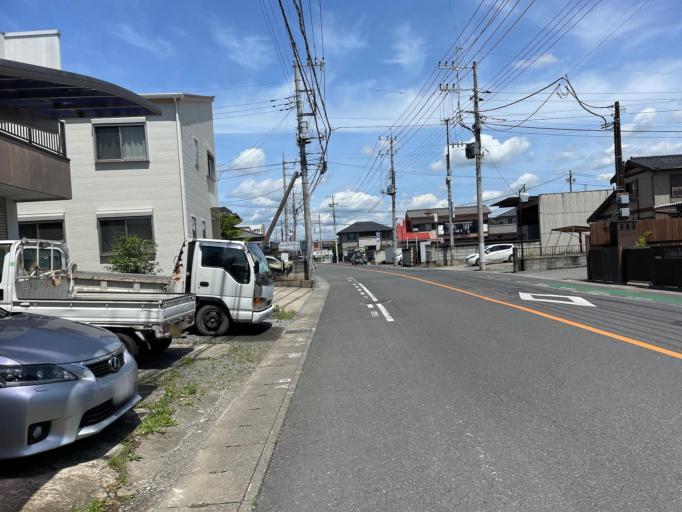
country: JP
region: Tochigi
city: Sano
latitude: 36.3152
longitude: 139.5848
